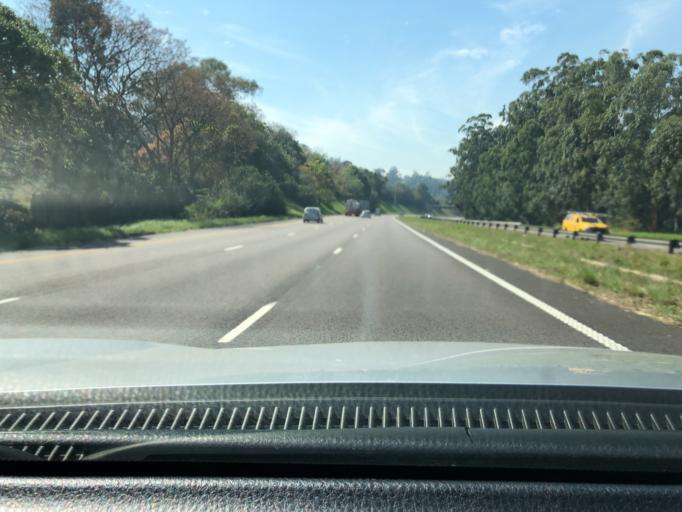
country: ZA
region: KwaZulu-Natal
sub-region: eThekwini Metropolitan Municipality
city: Berea
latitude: -29.8356
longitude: 30.8787
